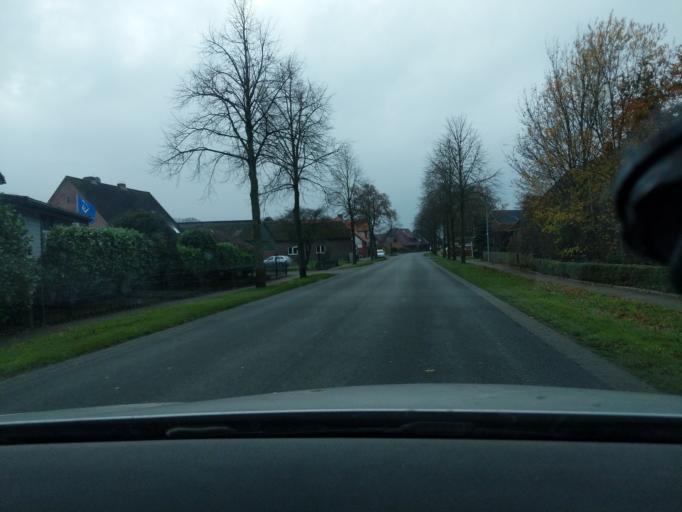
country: DE
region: Lower Saxony
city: Ahlerstedt
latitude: 53.3665
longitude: 9.4287
